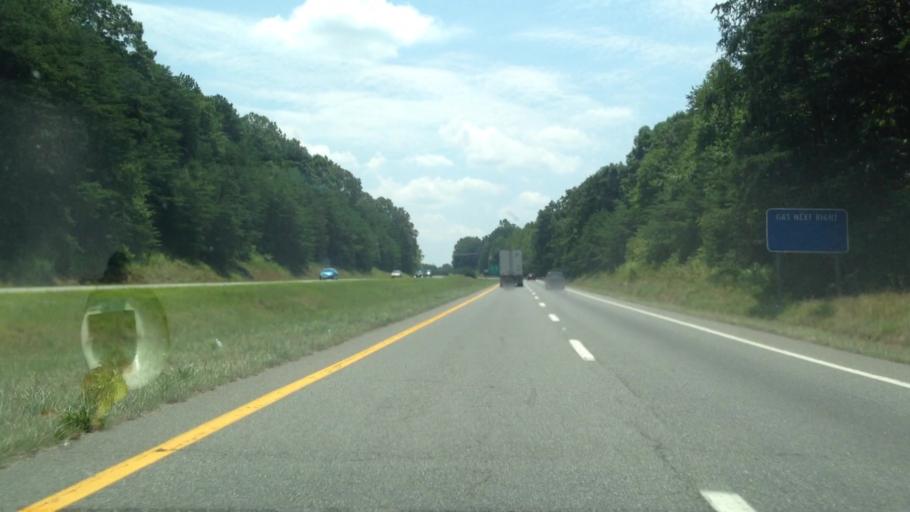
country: US
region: Virginia
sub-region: Henry County
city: Horse Pasture
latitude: 36.6543
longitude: -79.9221
